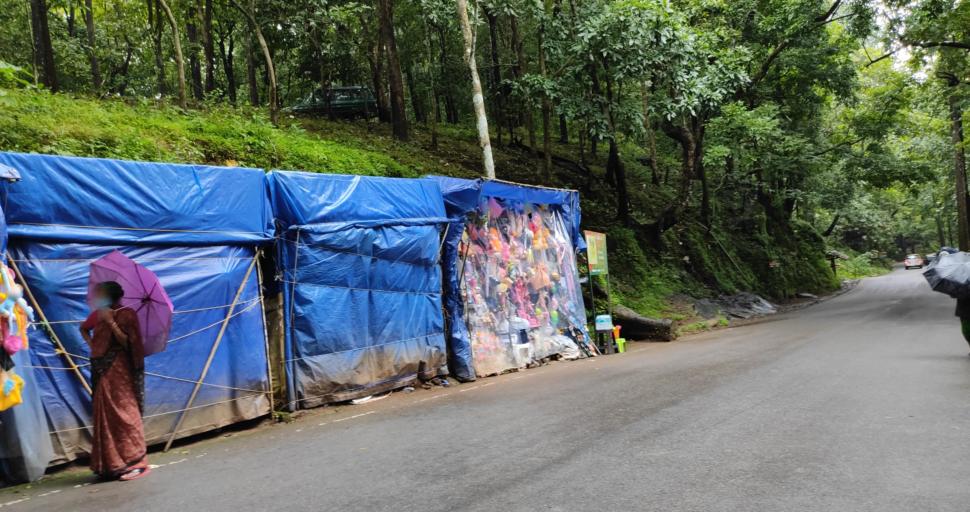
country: IN
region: Kerala
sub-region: Ernakulam
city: Angamali
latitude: 10.2891
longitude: 76.5691
